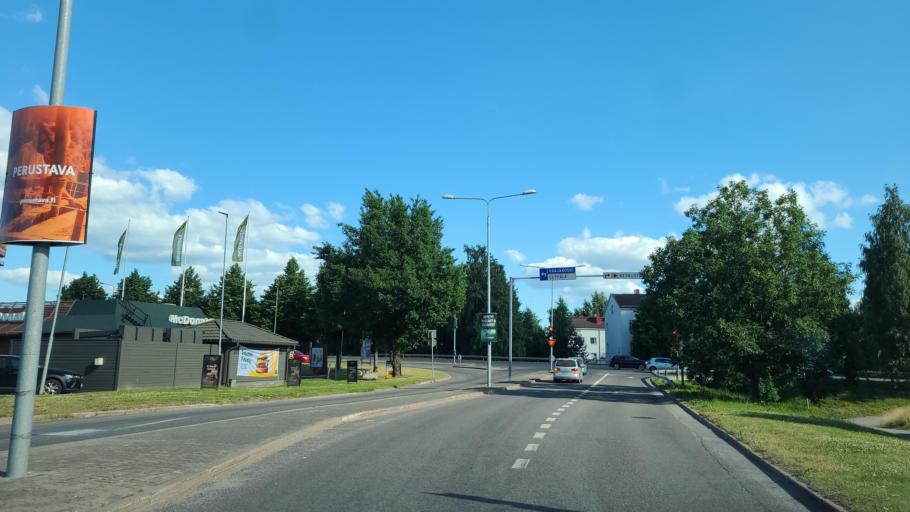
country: FI
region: Central Finland
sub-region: Jyvaeskylae
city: Jyvaeskylae
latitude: 62.2510
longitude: 25.7681
